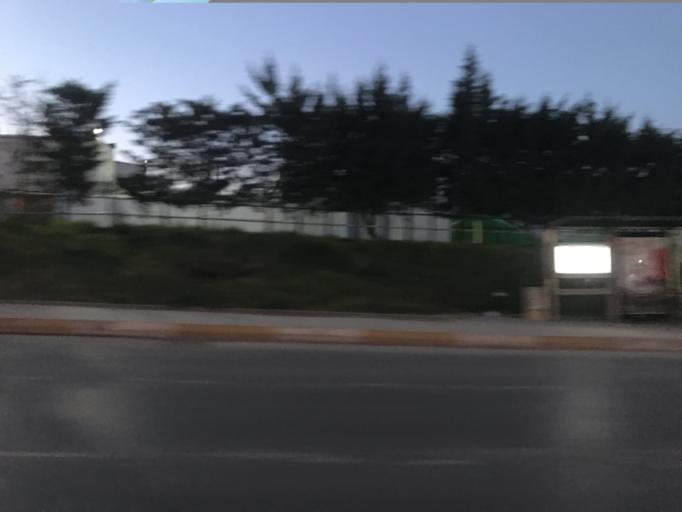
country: TR
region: Istanbul
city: Pendik
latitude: 40.8991
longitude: 29.2707
